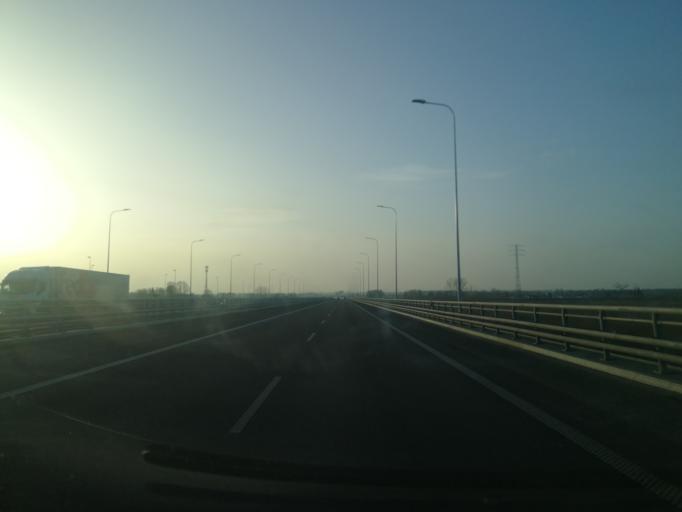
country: PL
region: Pomeranian Voivodeship
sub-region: Powiat nowodworski
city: Ostaszewo
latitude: 54.2576
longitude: 18.9445
